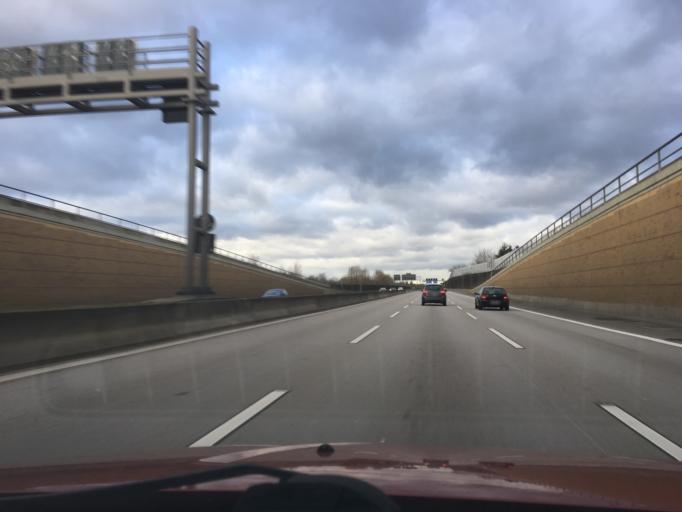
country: DE
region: Berlin
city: Rudow
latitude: 52.4430
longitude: 13.4791
